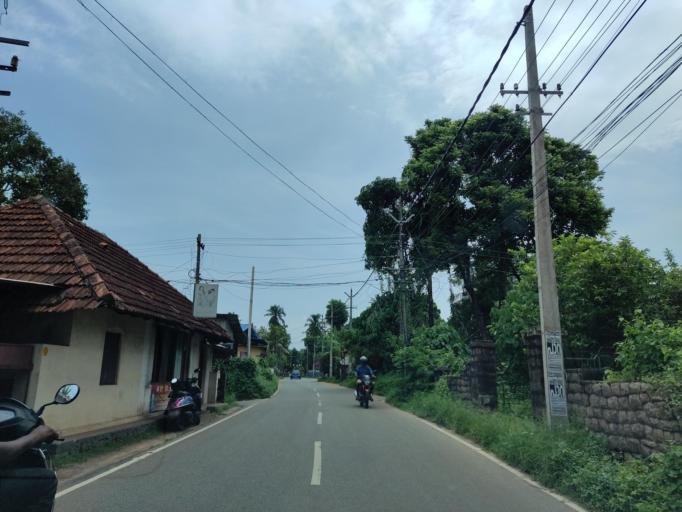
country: IN
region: Kerala
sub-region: Alappuzha
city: Chengannur
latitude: 9.3172
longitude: 76.6111
